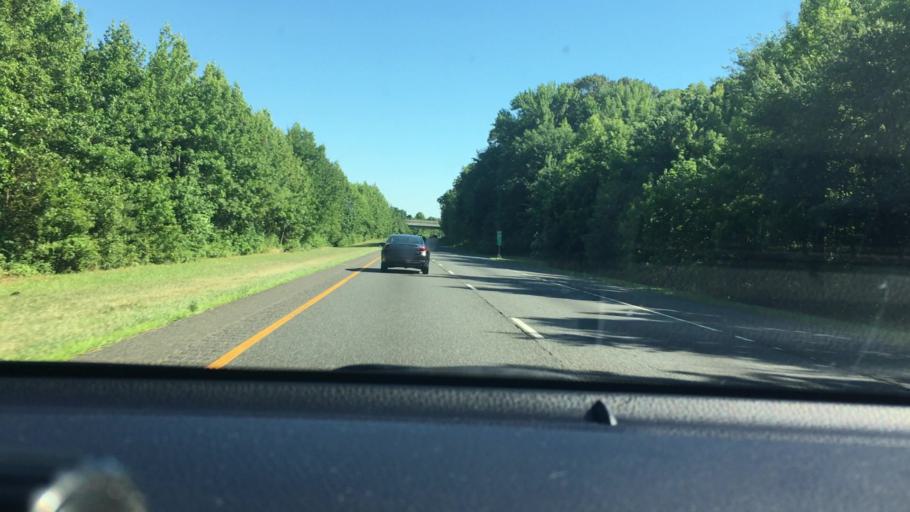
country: US
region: New Jersey
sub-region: Gloucester County
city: Wenonah
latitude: 39.7824
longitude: -75.1164
